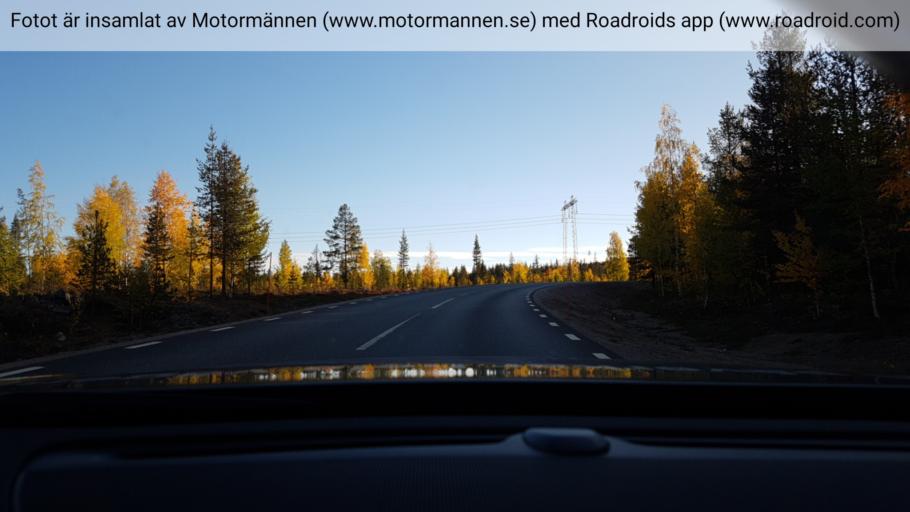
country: SE
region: Norrbotten
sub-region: Jokkmokks Kommun
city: Jokkmokk
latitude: 66.8043
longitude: 19.8773
